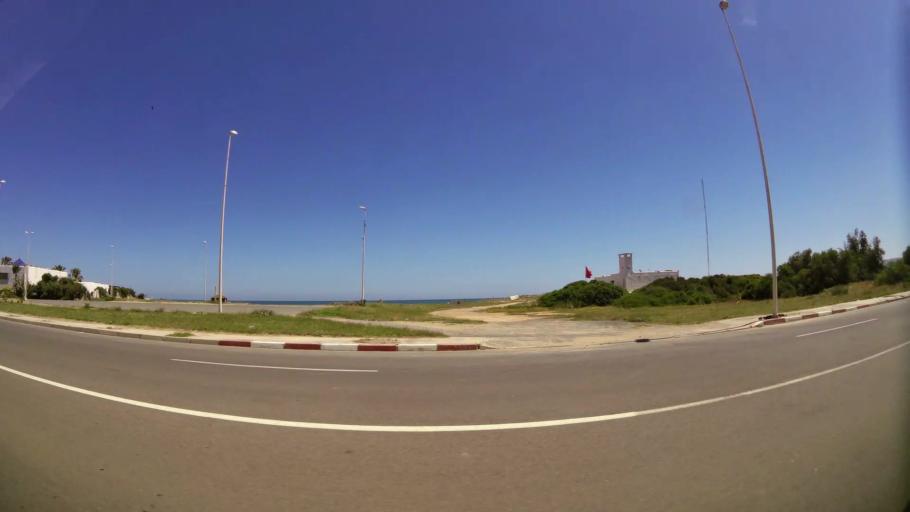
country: MA
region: Oriental
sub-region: Berkane-Taourirt
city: Madagh
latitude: 35.0956
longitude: -2.2613
